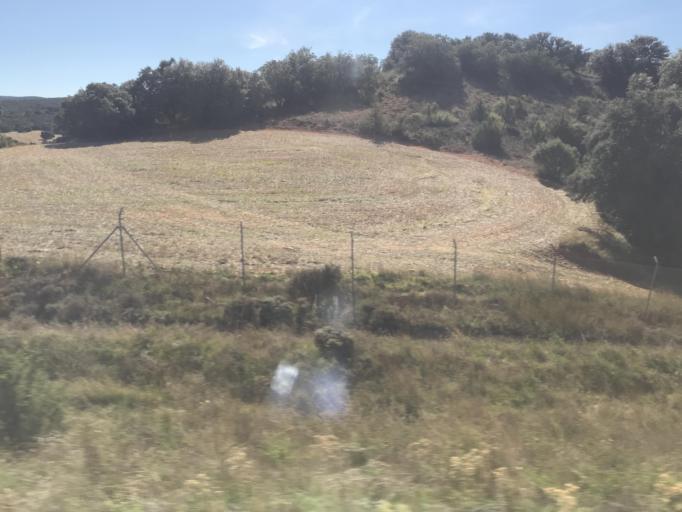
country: ES
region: Castille and Leon
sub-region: Provincia de Soria
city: Arcos de Jalon
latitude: 41.1753
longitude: -2.2477
